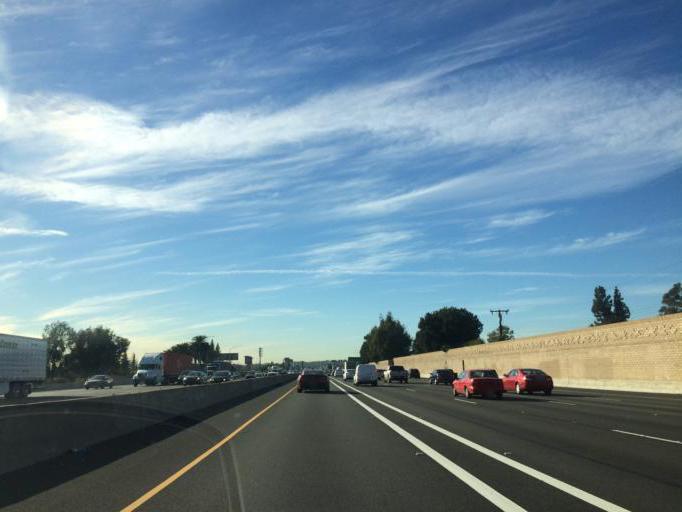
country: US
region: California
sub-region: Los Angeles County
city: Claremont
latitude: 34.0819
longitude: -117.7126
